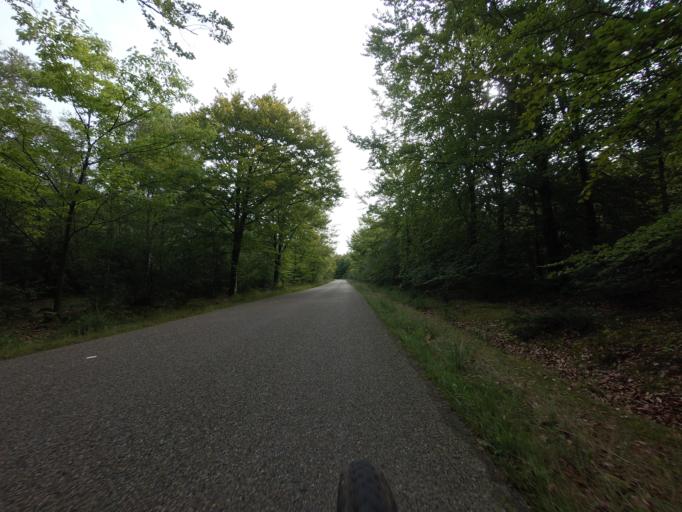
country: DK
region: North Denmark
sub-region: Hjorring Kommune
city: Hirtshals
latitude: 57.5792
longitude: 10.0709
